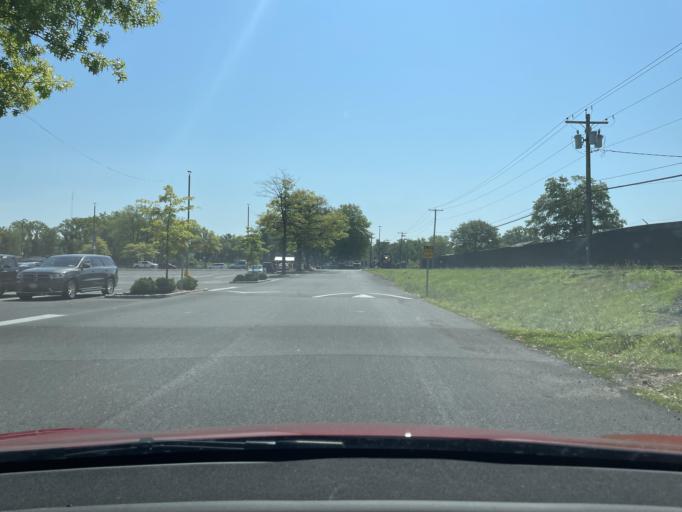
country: US
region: New York
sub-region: Ulster County
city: Kingston
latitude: 41.9359
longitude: -74.0170
